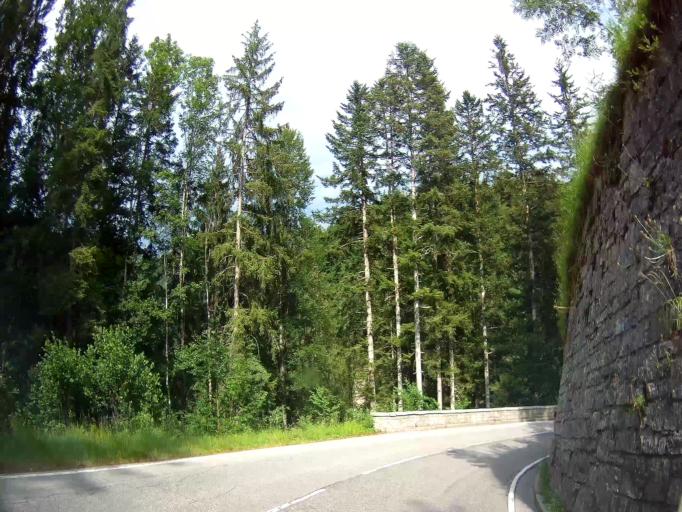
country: DE
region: Bavaria
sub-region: Upper Bavaria
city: Berchtesgaden
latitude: 47.6325
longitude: 13.0583
